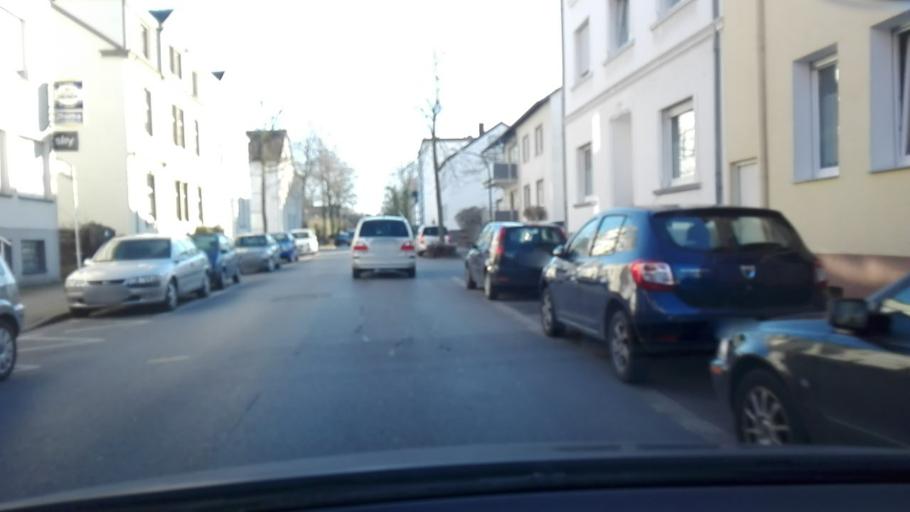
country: DE
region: North Rhine-Westphalia
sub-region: Regierungsbezirk Arnsberg
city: Holzwickede
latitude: 51.5032
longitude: 7.6204
